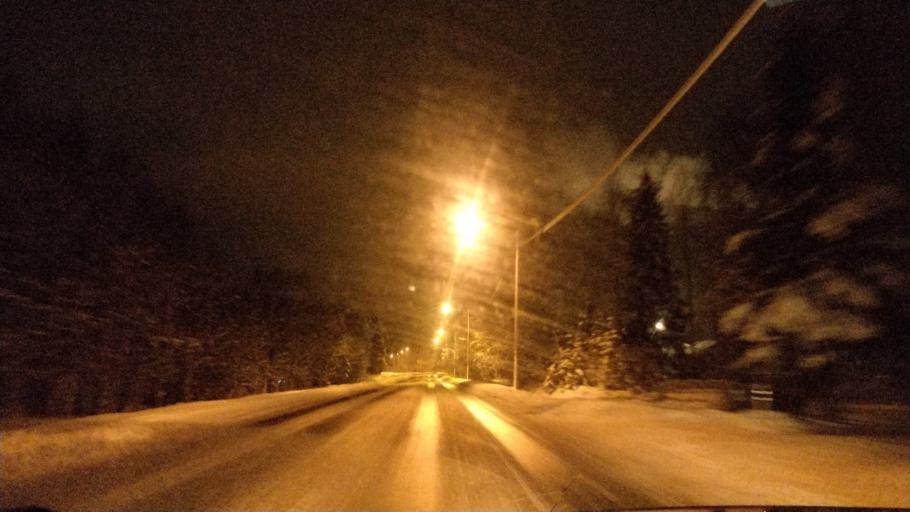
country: FI
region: Lapland
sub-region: Rovaniemi
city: Rovaniemi
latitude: 66.3821
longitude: 25.3784
